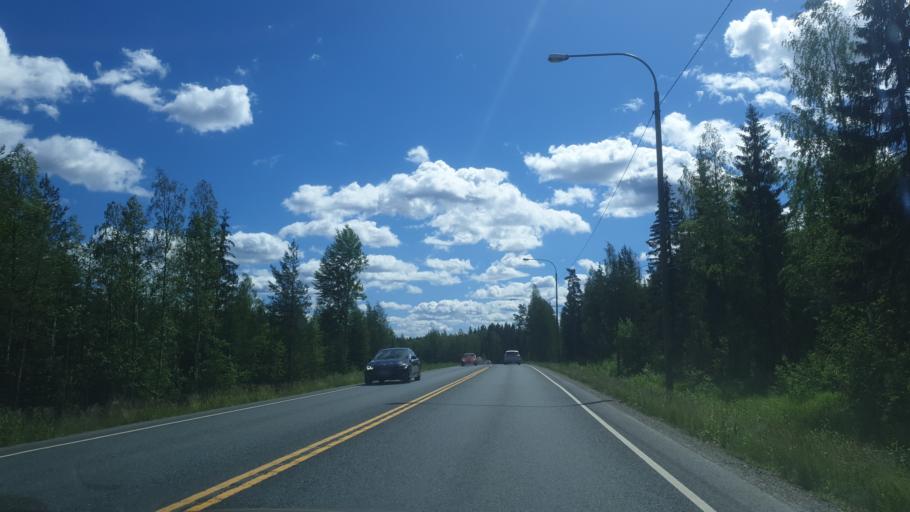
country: FI
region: Northern Savo
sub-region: Varkaus
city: Leppaevirta
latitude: 62.5419
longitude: 27.6307
